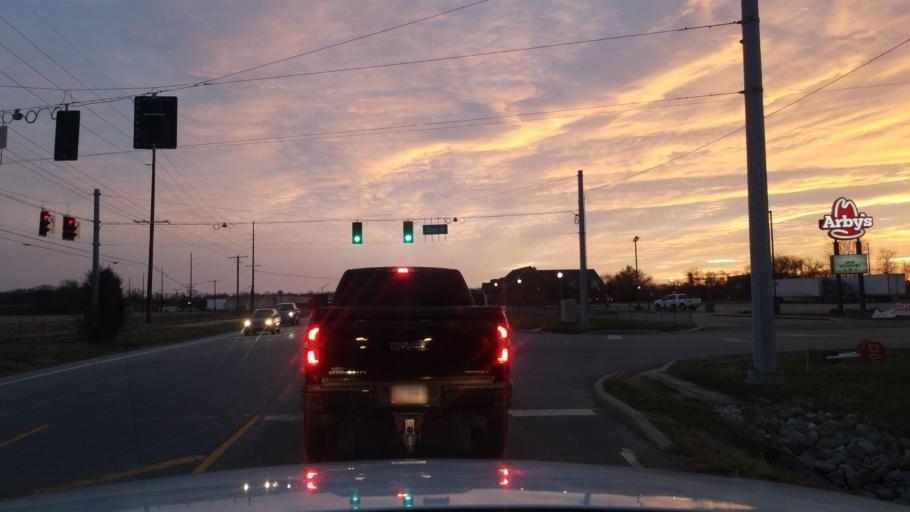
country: US
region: Indiana
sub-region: Posey County
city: Mount Vernon
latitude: 37.9364
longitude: -87.8791
